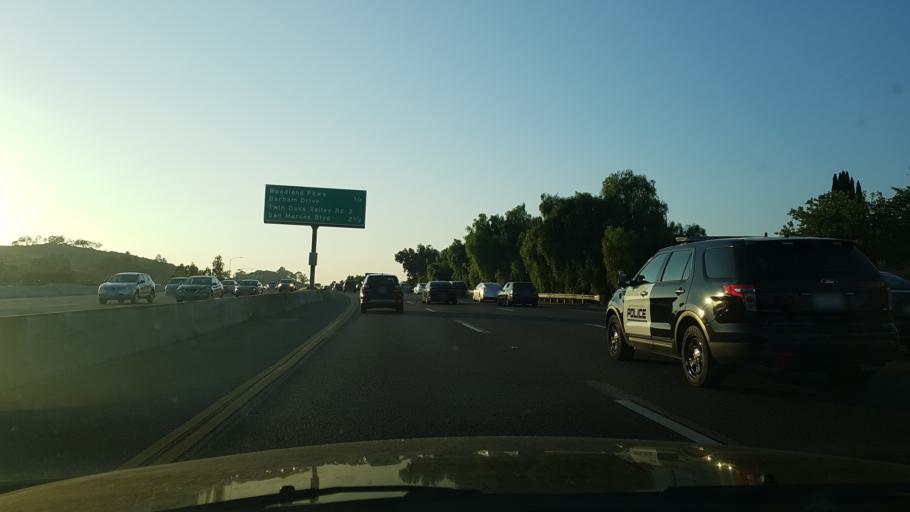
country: US
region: California
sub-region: San Diego County
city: San Marcos
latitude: 33.1344
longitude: -117.1268
